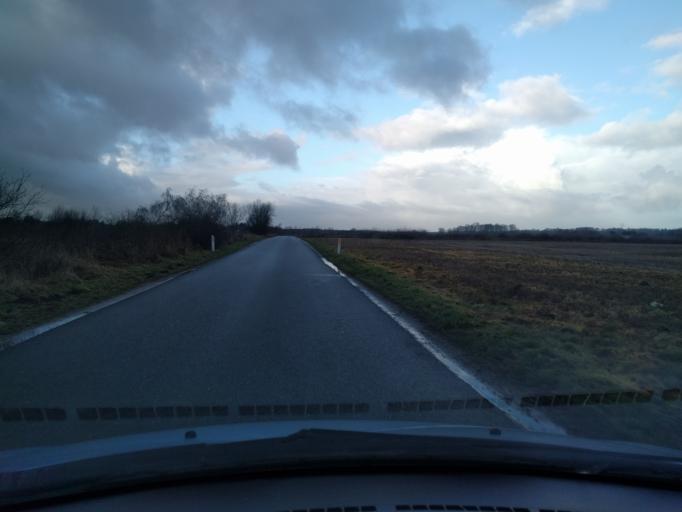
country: DK
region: South Denmark
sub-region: Kerteminde Kommune
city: Langeskov
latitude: 55.3777
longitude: 10.5804
